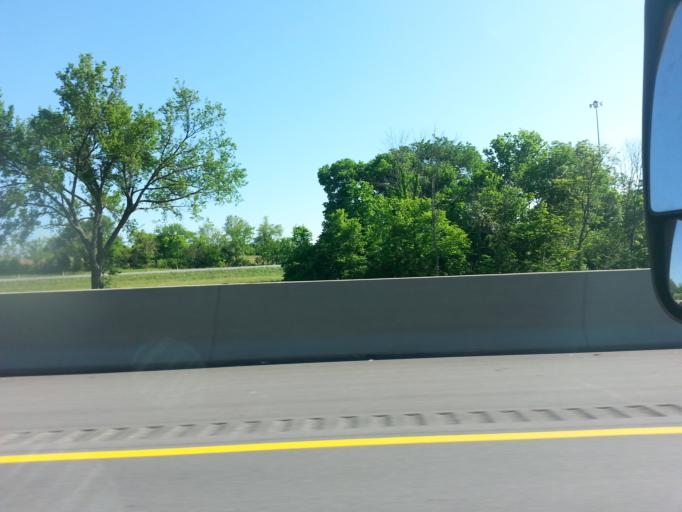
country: US
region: Kentucky
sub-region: Shelby County
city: Shelbyville
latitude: 38.1926
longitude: -85.2731
